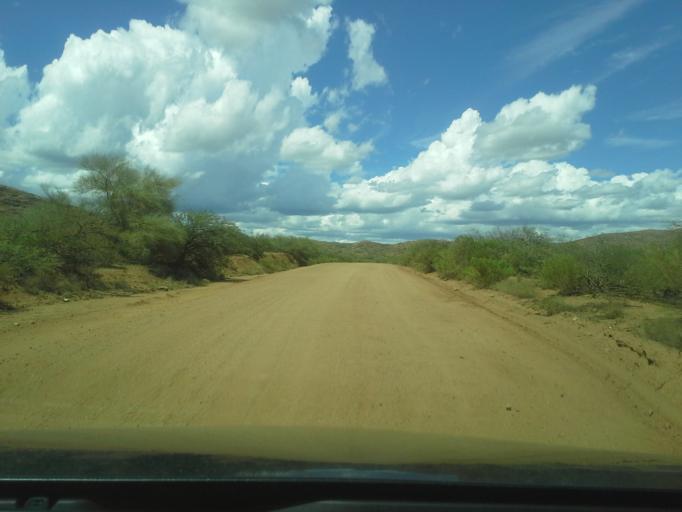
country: US
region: Arizona
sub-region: Yavapai County
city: Spring Valley
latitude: 34.2606
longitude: -112.1801
